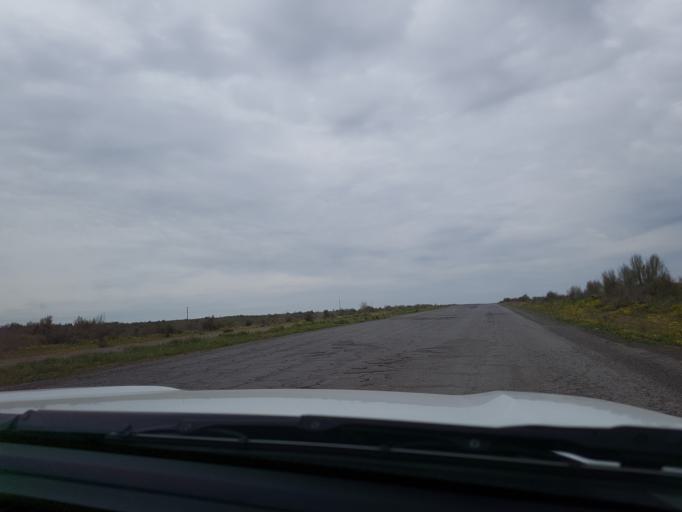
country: TM
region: Mary
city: Bayramaly
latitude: 37.9122
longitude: 62.6212
